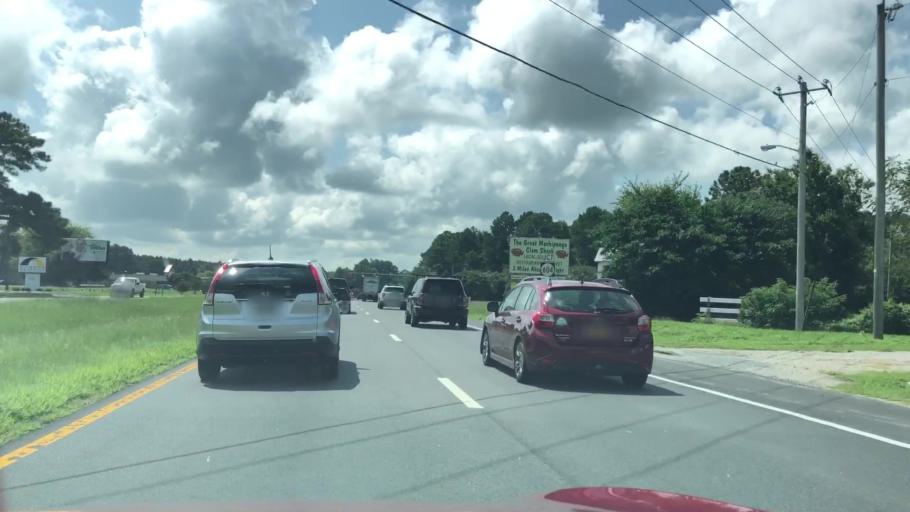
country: US
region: Virginia
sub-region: Northampton County
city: Exmore
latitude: 37.5192
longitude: -75.8320
